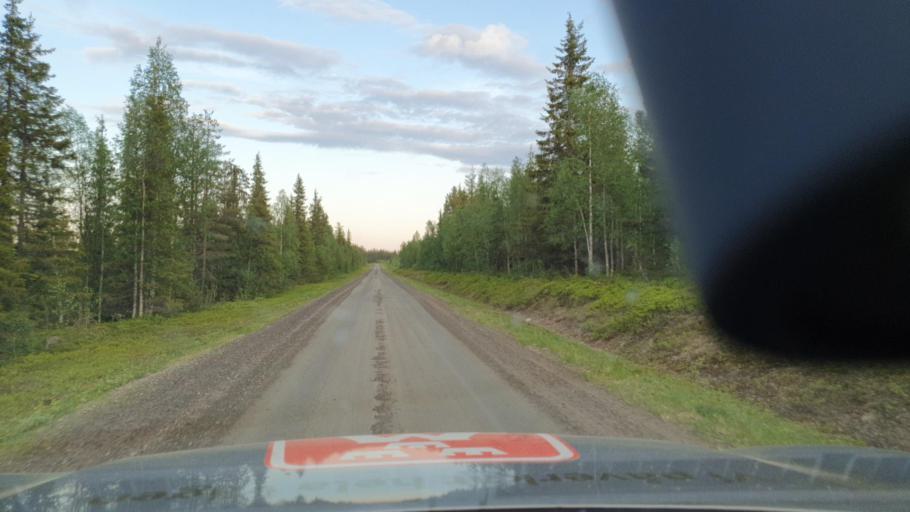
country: SE
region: Norrbotten
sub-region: Bodens Kommun
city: Boden
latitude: 66.5271
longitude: 21.4894
